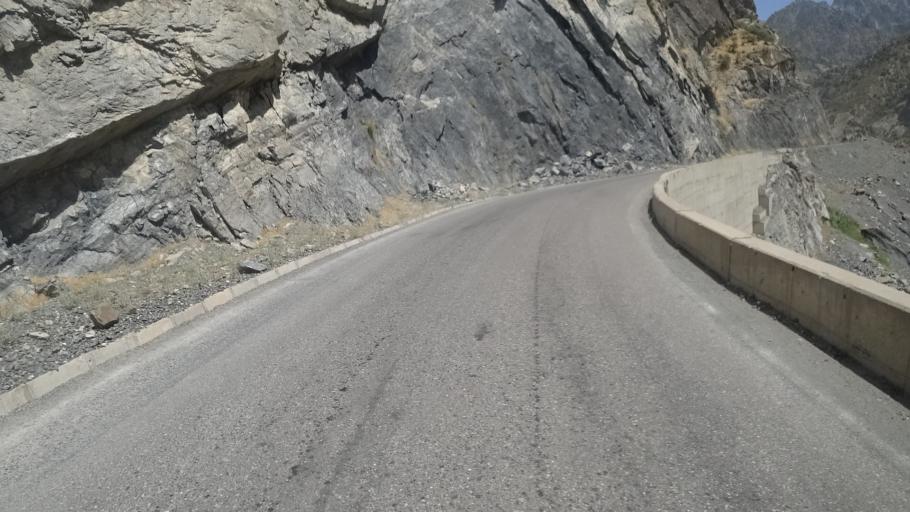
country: AF
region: Badakhshan
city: Deh Khwahan
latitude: 38.0004
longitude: 70.3190
